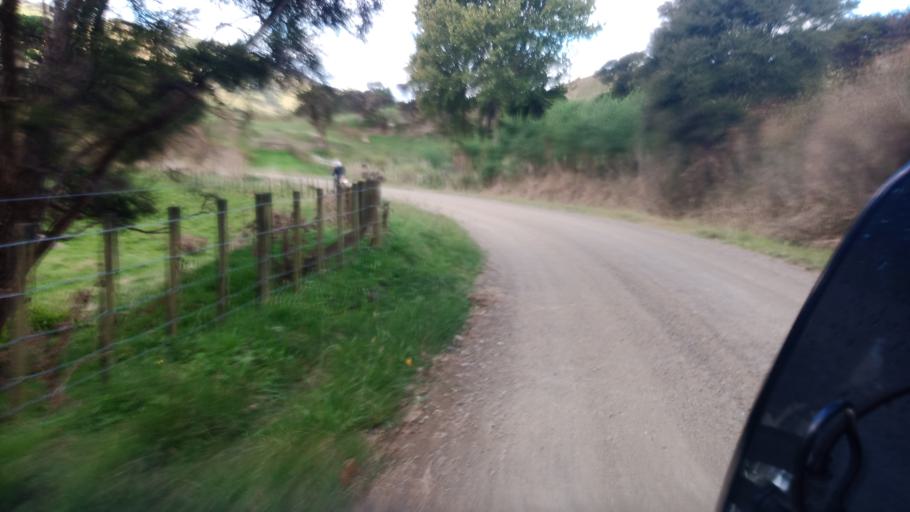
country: NZ
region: Gisborne
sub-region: Gisborne District
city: Gisborne
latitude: -38.4606
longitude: 177.6369
